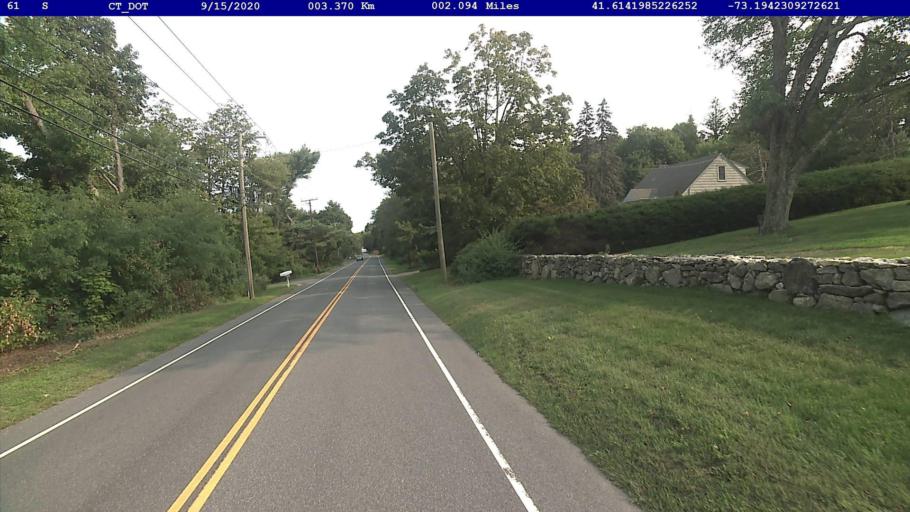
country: US
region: Connecticut
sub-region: Litchfield County
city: Bethlehem Village
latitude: 41.6142
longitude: -73.1943
